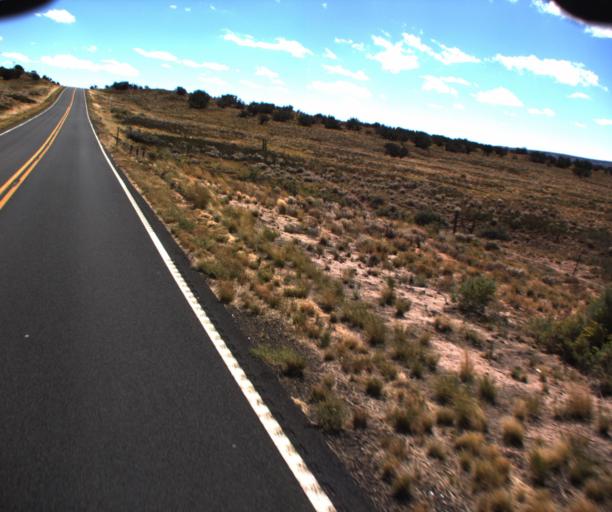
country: US
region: Arizona
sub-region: Apache County
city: Houck
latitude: 35.0764
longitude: -109.2967
